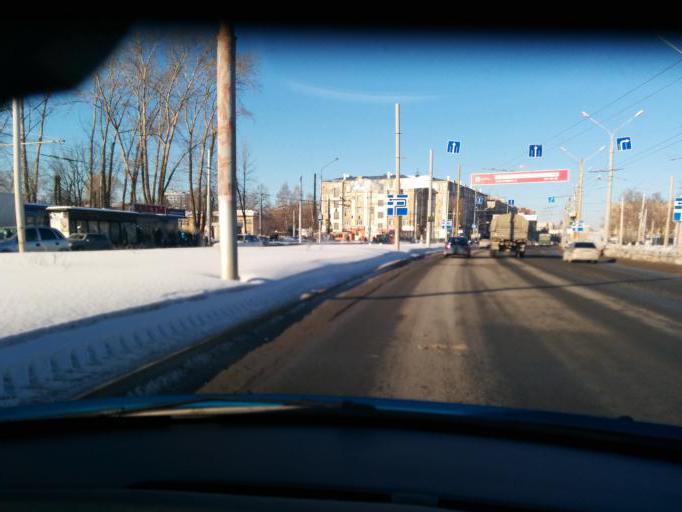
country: RU
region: Perm
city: Perm
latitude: 57.9842
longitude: 56.2581
